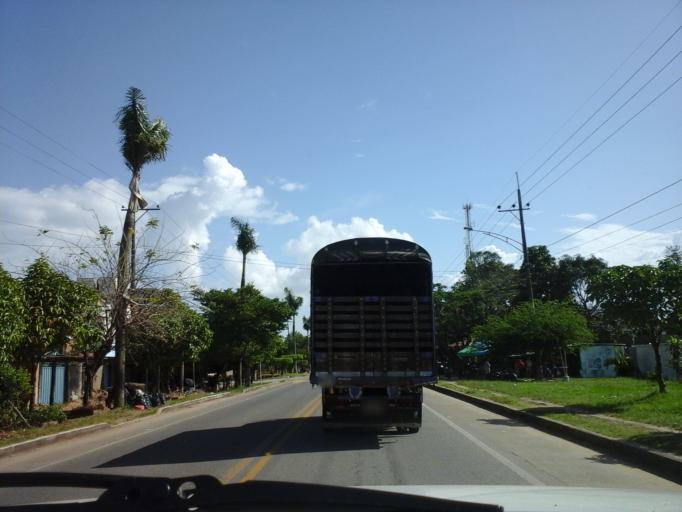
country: CO
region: Meta
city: Puerto Lopez
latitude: 4.0896
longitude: -72.9583
